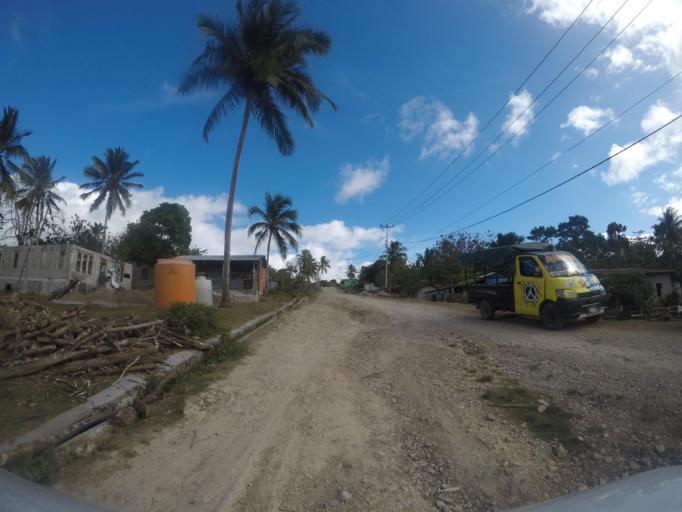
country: TL
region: Lautem
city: Lospalos
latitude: -8.5718
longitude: 126.8841
